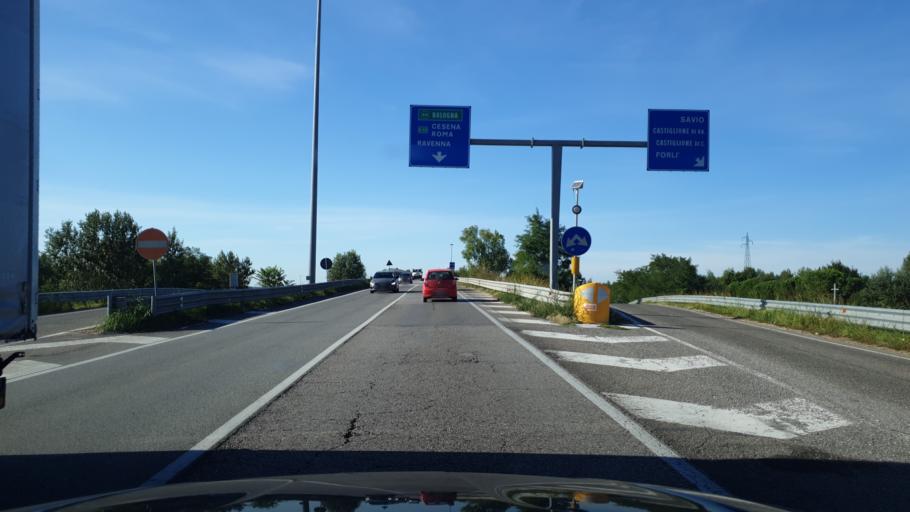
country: IT
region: Emilia-Romagna
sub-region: Provincia di Ravenna
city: Savio
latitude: 44.3008
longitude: 12.2920
